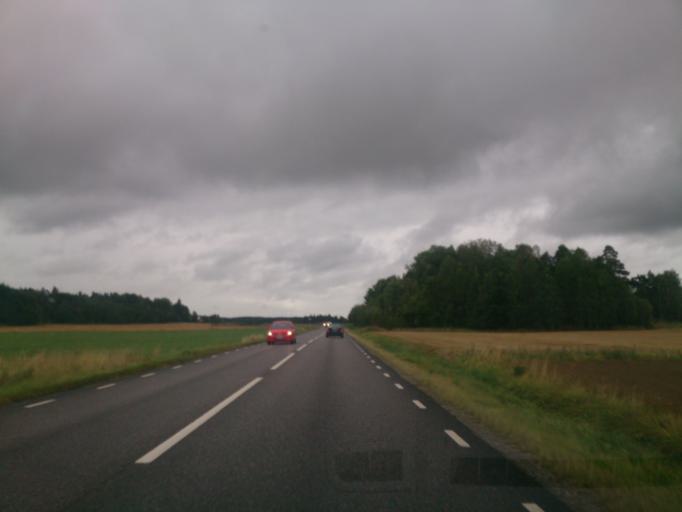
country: SE
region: OEstergoetland
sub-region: Norrkopings Kommun
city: Krokek
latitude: 58.5658
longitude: 16.5942
